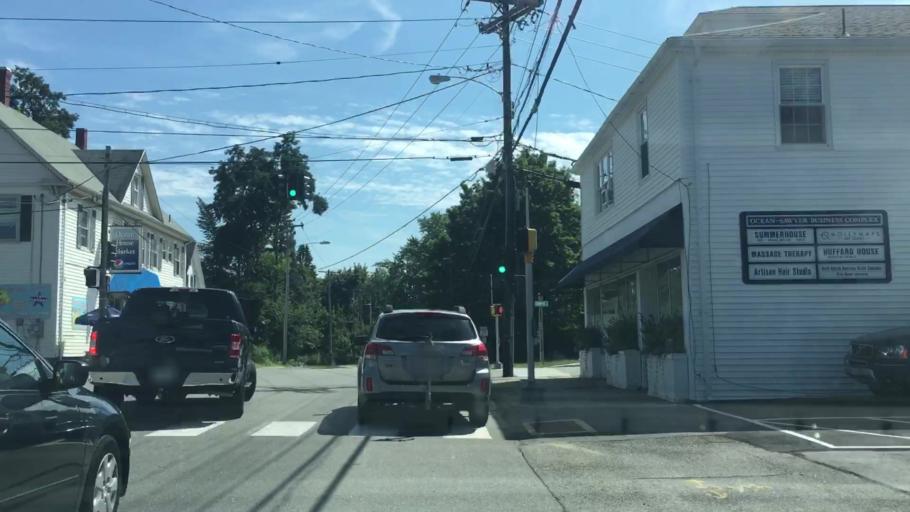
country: US
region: Maine
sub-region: Cumberland County
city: South Portland
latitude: 43.6251
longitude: -70.2501
